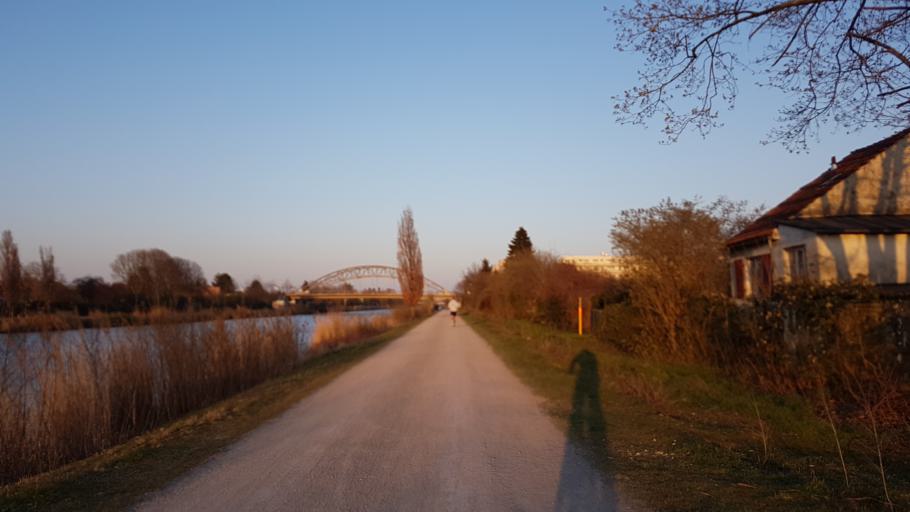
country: DE
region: Lower Saxony
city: Hannover
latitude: 52.4048
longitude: 9.7592
